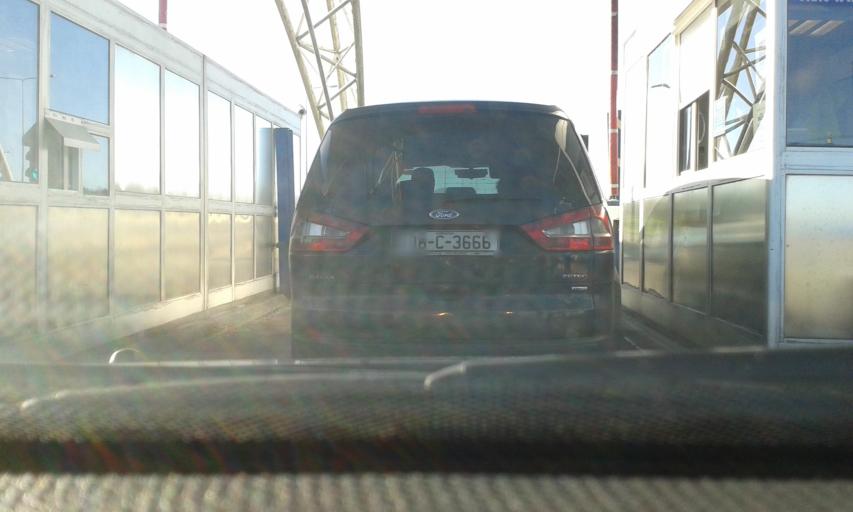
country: IE
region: Leinster
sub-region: Laois
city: Mountrath
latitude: 53.0002
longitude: -7.3931
